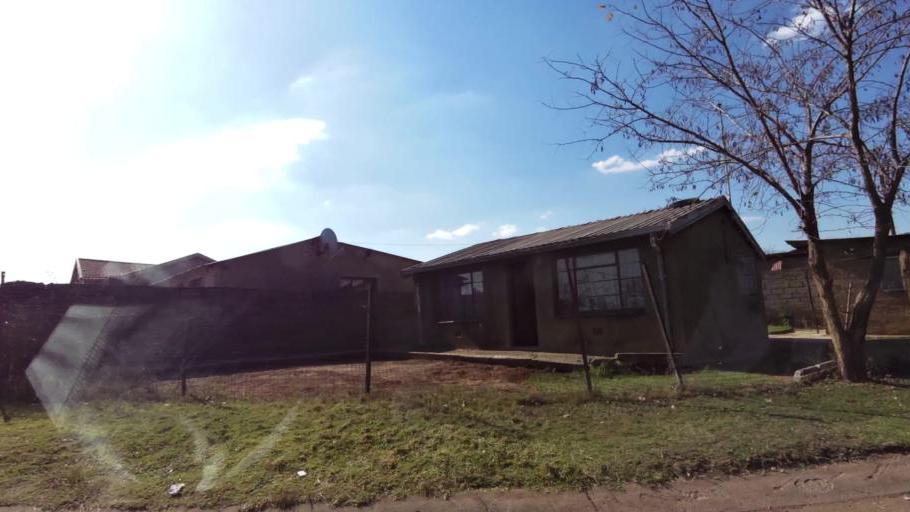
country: ZA
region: Gauteng
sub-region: City of Johannesburg Metropolitan Municipality
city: Soweto
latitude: -26.2378
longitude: 27.8773
